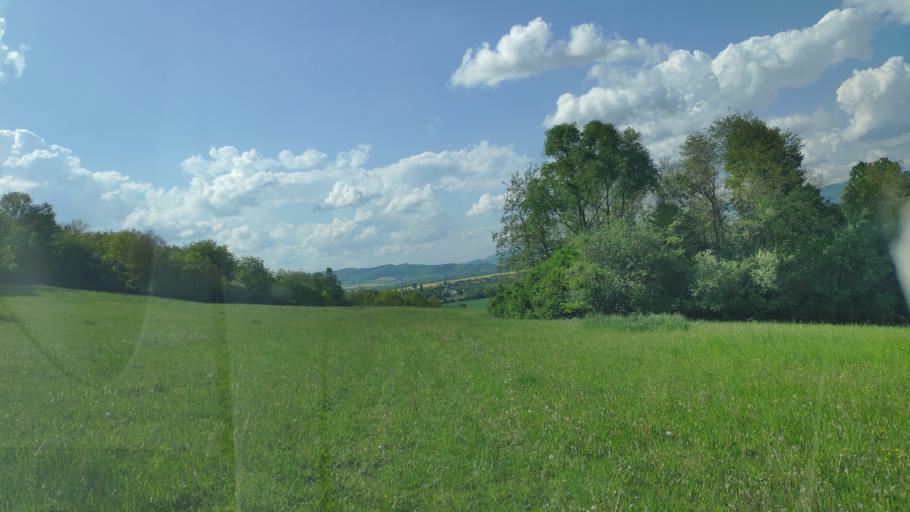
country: SK
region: Presovsky
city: Sabinov
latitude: 49.0507
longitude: 21.1535
